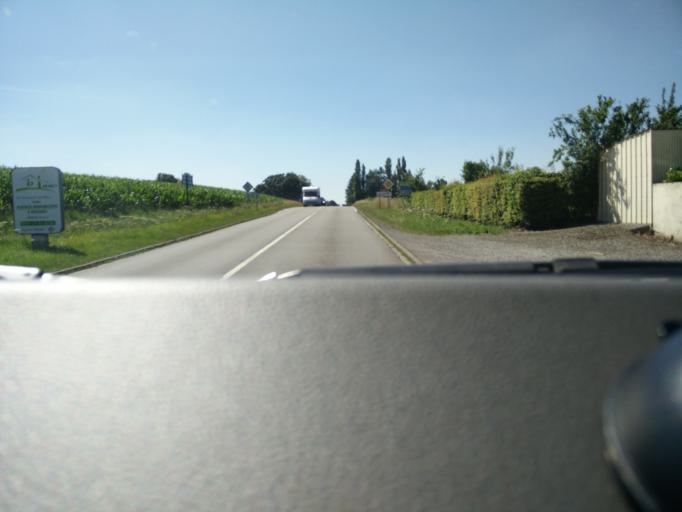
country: FR
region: Nord-Pas-de-Calais
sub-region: Departement du Nord
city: Avesnelles
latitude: 50.1729
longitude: 3.9530
